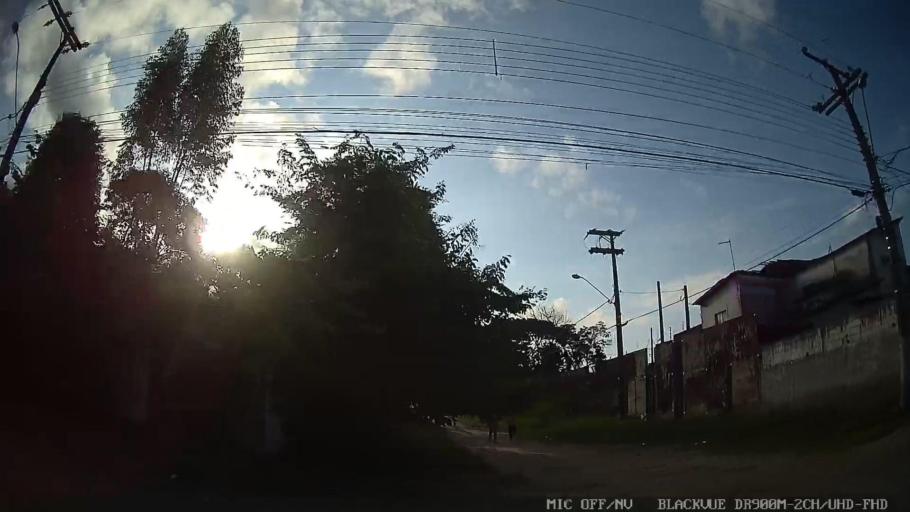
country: BR
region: Sao Paulo
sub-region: Itanhaem
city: Itanhaem
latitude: -24.1493
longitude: -46.8186
